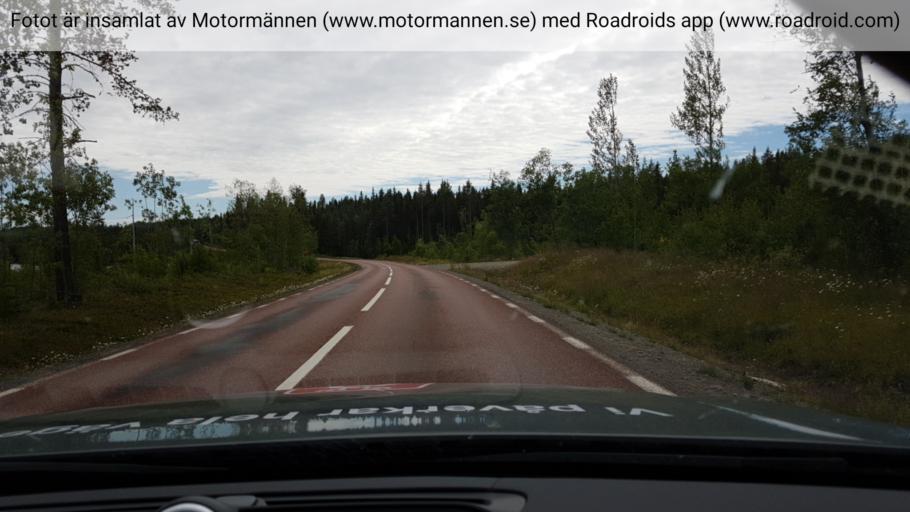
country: SE
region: Vaesterbotten
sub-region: Dorotea Kommun
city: Dorotea
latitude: 64.0637
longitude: 16.0453
